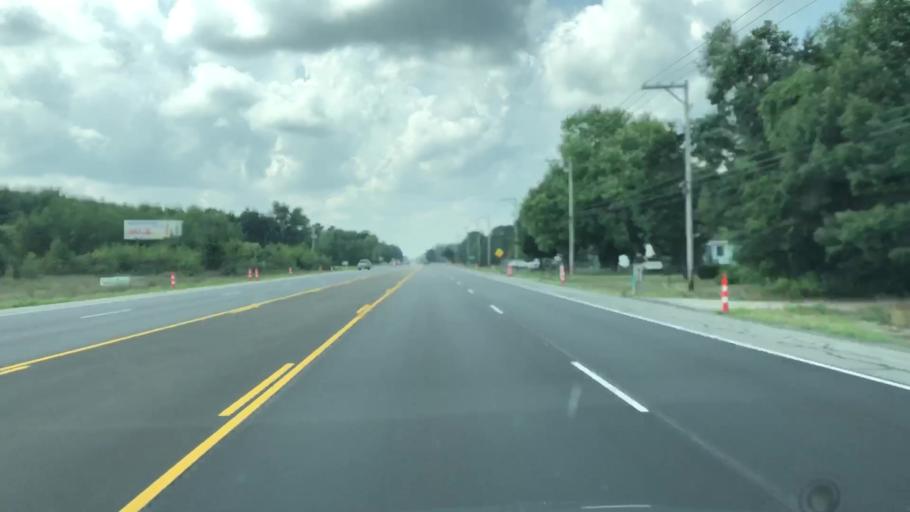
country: US
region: Michigan
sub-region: Isabella County
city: Shepherd
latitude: 43.6118
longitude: -84.6230
